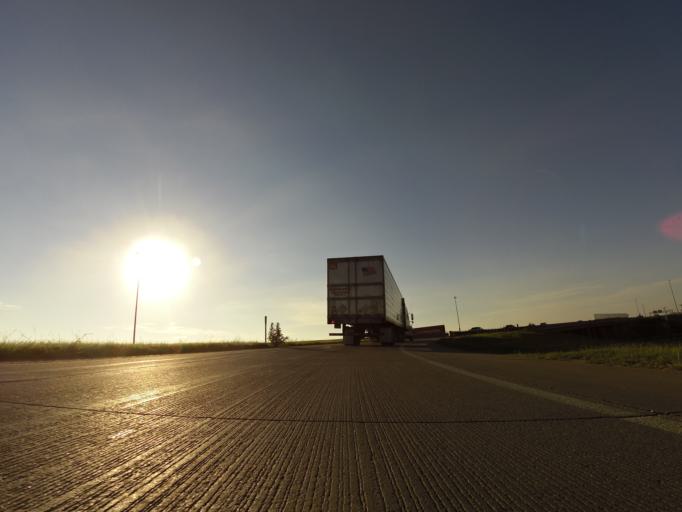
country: US
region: Kansas
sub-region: Sedgwick County
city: Wichita
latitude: 37.7394
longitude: -97.3196
